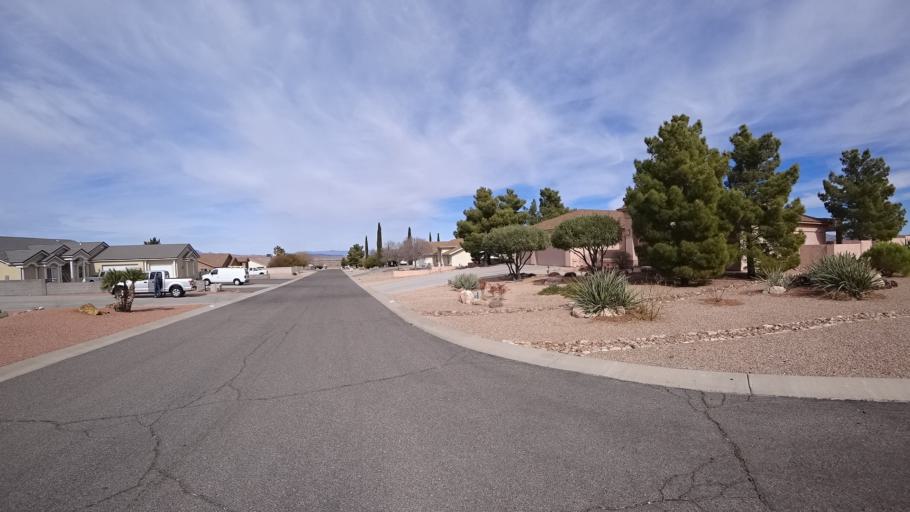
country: US
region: Arizona
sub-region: Mohave County
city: Kingman
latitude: 35.1929
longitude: -113.9770
